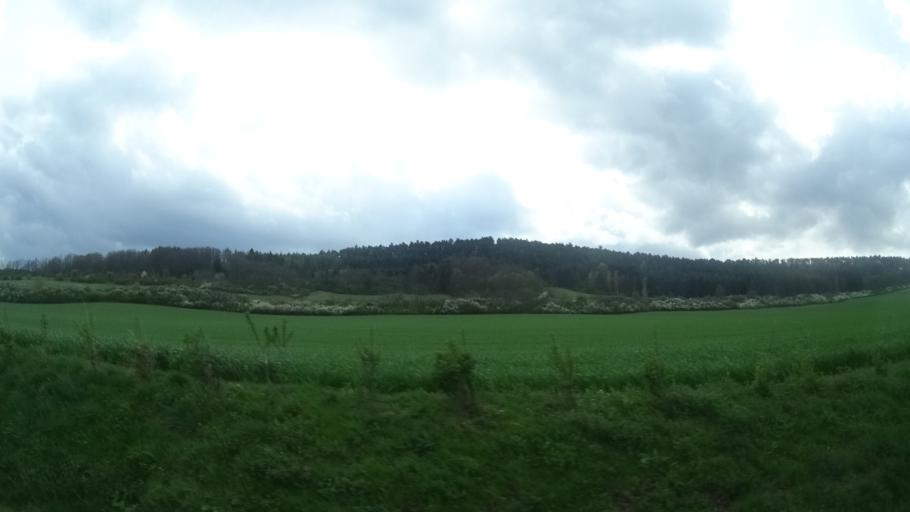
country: DE
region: Thuringia
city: Arnstadt
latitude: 50.8422
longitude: 10.9137
